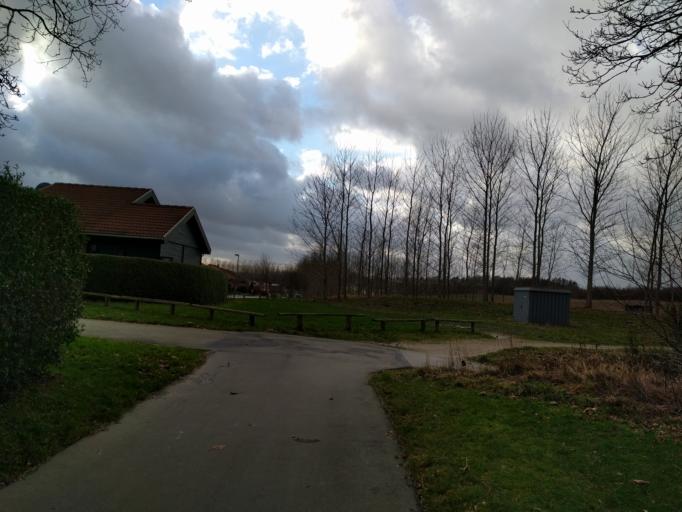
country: DK
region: Central Jutland
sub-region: Silkeborg Kommune
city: Silkeborg
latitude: 56.1893
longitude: 9.5158
